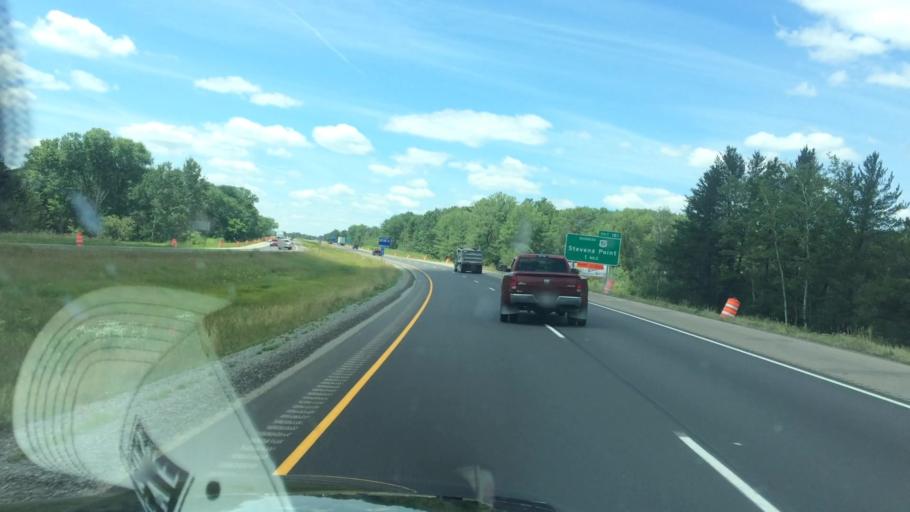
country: US
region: Wisconsin
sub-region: Portage County
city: Stevens Point
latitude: 44.5482
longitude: -89.5550
